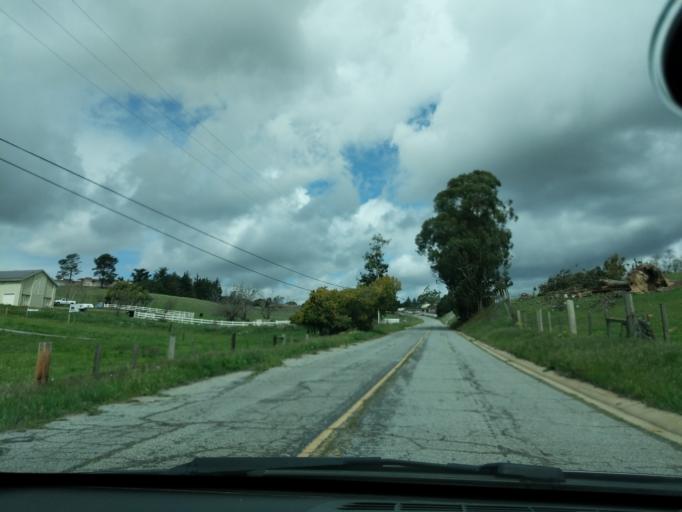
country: US
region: California
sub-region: Monterey County
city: Prunedale
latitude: 36.7579
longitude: -121.6571
